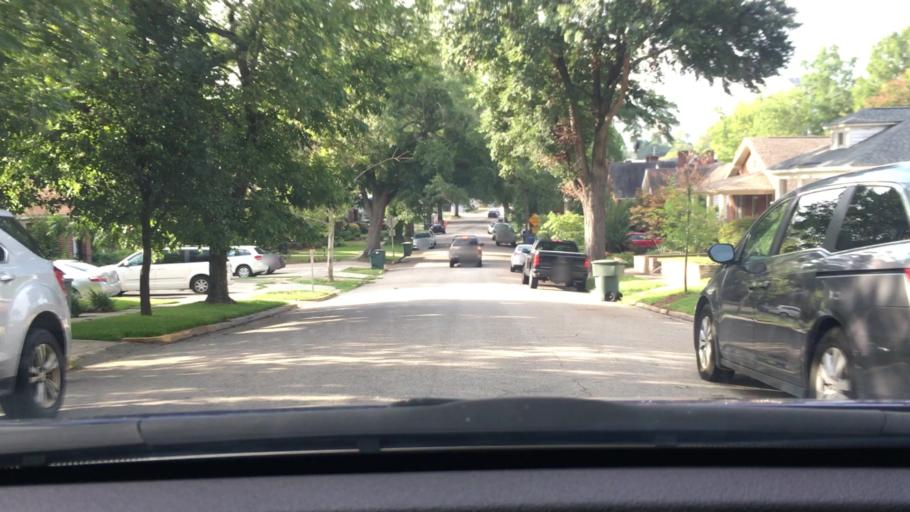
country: US
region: South Carolina
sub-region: Richland County
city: Columbia
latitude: 34.0187
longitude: -81.0399
